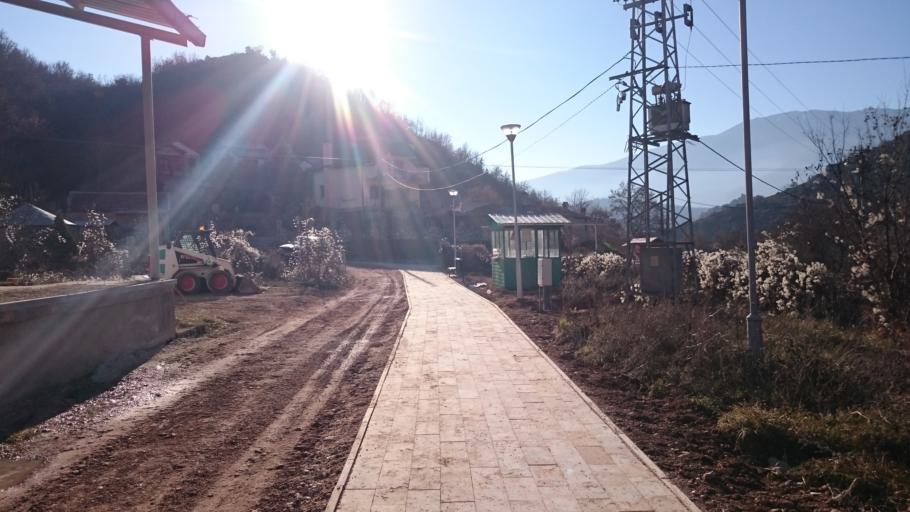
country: MK
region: Makedonski Brod
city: Makedonski Brod
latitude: 41.5459
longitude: 21.2499
